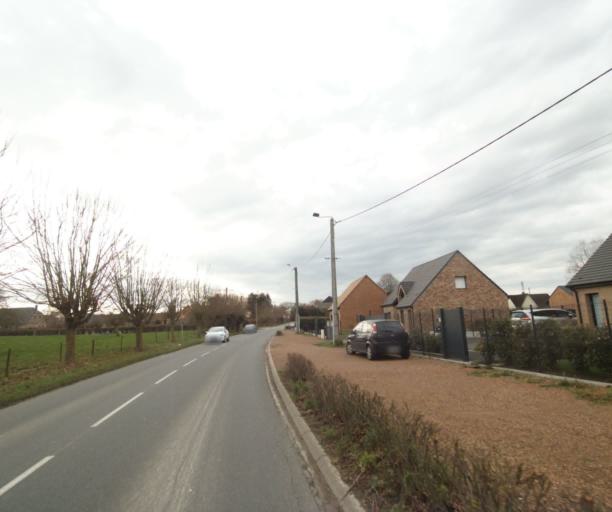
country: FR
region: Nord-Pas-de-Calais
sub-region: Departement du Nord
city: Sebourg
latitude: 50.3434
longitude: 3.6398
